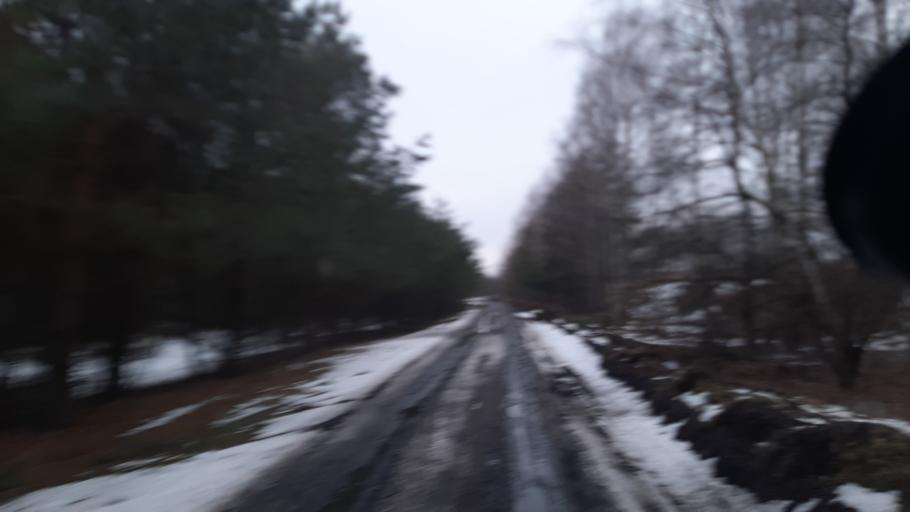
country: PL
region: Lublin Voivodeship
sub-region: Powiat wlodawski
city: Wlodawa
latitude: 51.5142
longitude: 23.6088
